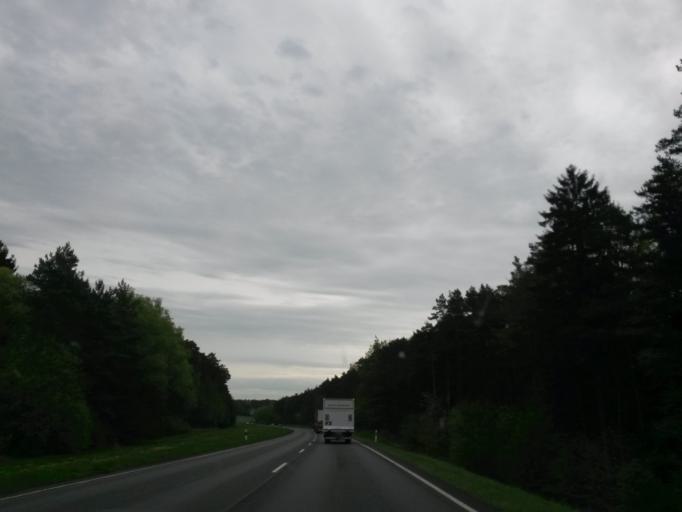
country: DE
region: Bavaria
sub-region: Upper Franconia
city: Pommersfelden
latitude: 49.7576
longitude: 10.8671
